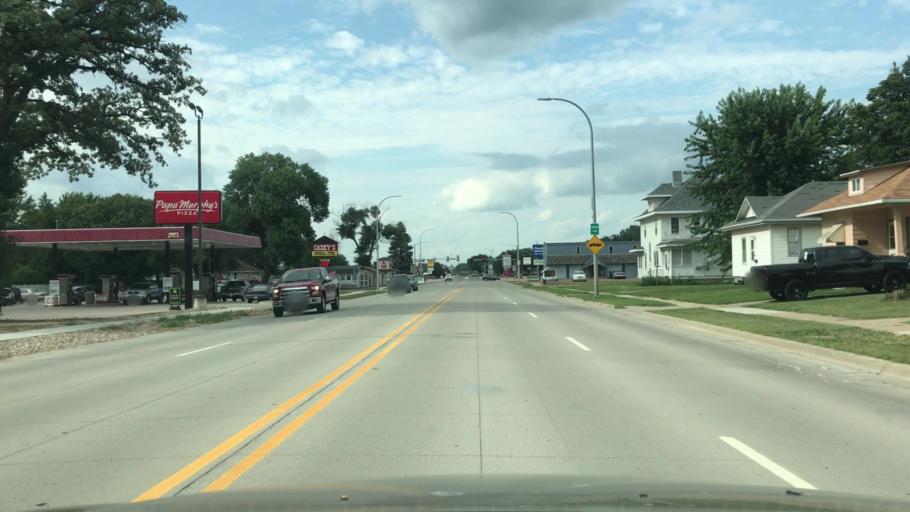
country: US
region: Iowa
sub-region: Plymouth County
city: Le Mars
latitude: 42.7909
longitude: -96.1738
